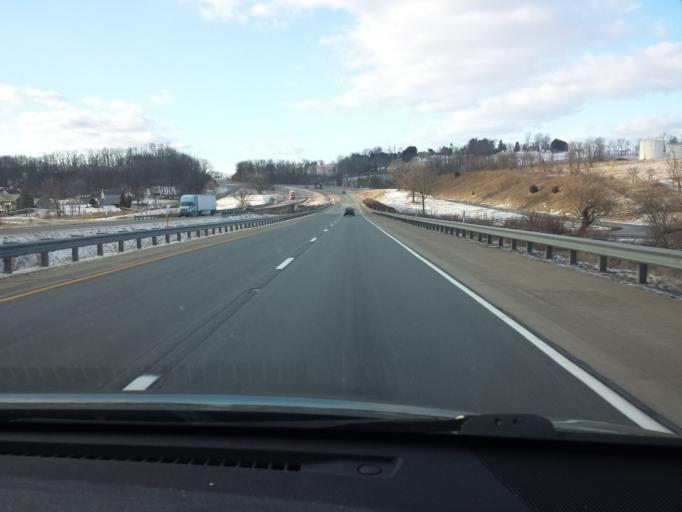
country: US
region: Pennsylvania
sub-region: Northumberland County
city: Milton
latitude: 41.0190
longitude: -76.7909
